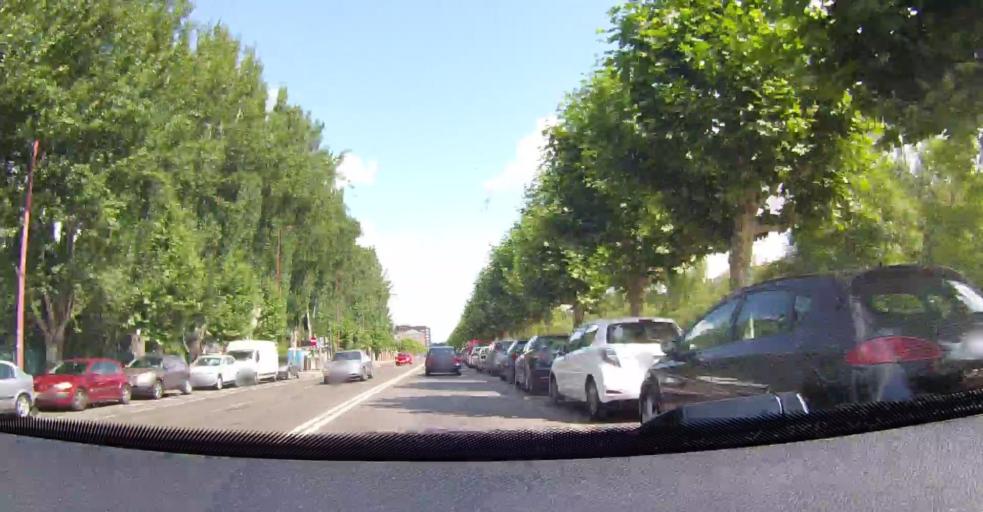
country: ES
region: Castille and Leon
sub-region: Provincia de Leon
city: Leon
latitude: 42.5904
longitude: -5.5771
